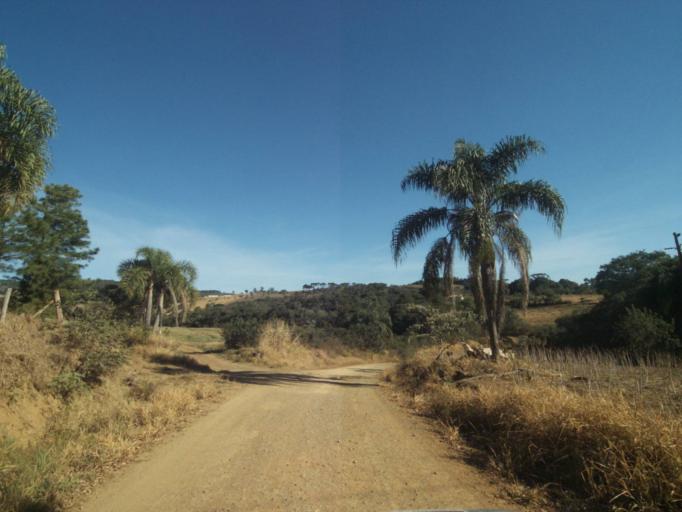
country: BR
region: Parana
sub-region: Tibagi
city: Tibagi
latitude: -24.5457
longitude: -50.5105
